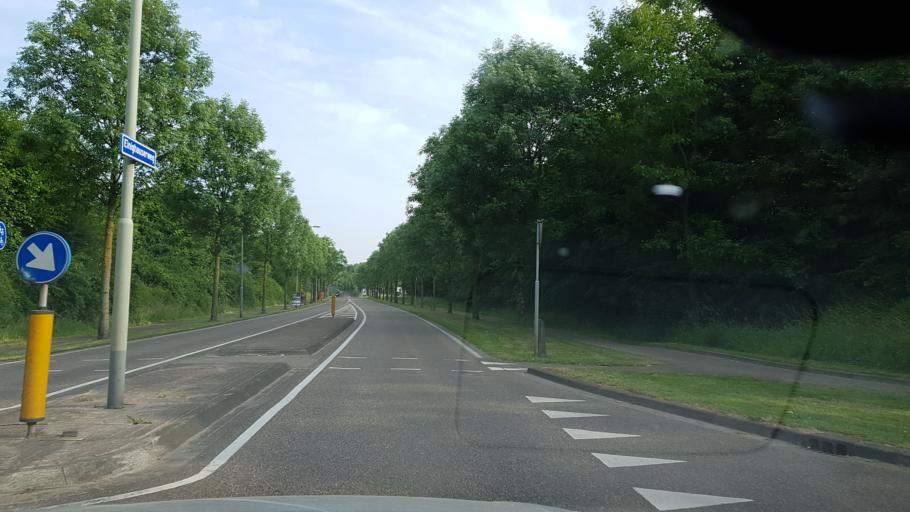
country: NL
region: Limburg
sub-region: Gemeente Sittard-Geleen
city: Limbricht
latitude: 50.9879
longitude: 5.8252
